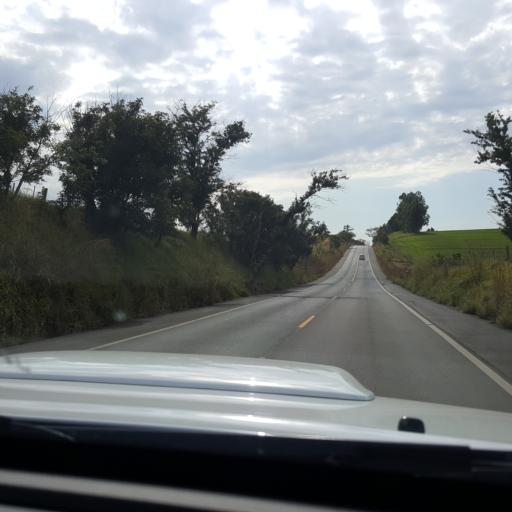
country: BR
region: Sao Paulo
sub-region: Itaporanga
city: Itaporanga
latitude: -23.7536
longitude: -49.4519
